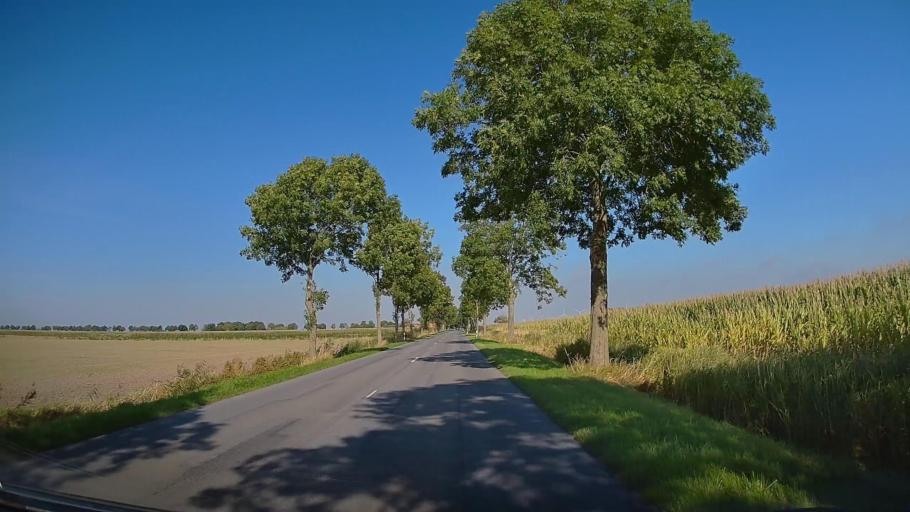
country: DE
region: Lower Saxony
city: Wremen
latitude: 53.6185
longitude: 8.5285
